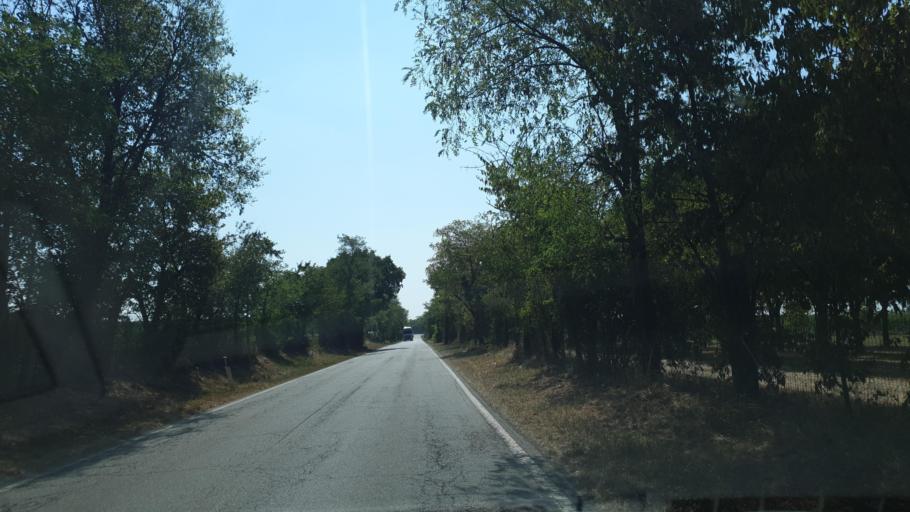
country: IT
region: Lombardy
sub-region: Provincia di Brescia
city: Carzago Riviera
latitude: 45.5022
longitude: 10.4649
